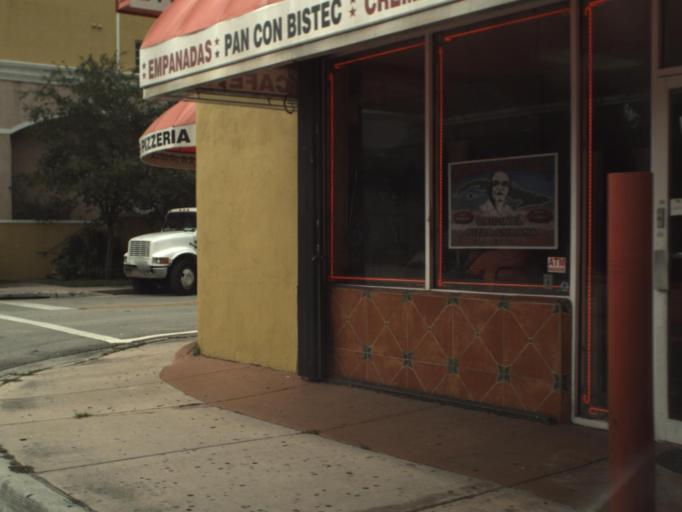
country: US
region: Florida
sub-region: Miami-Dade County
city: West Miami
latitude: 25.7639
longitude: -80.2805
